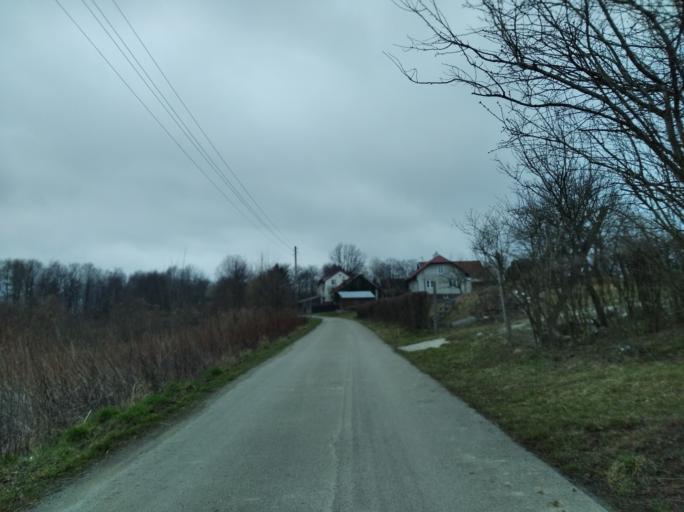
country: PL
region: Subcarpathian Voivodeship
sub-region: Powiat strzyzowski
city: Strzyzow
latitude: 49.8853
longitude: 21.7952
